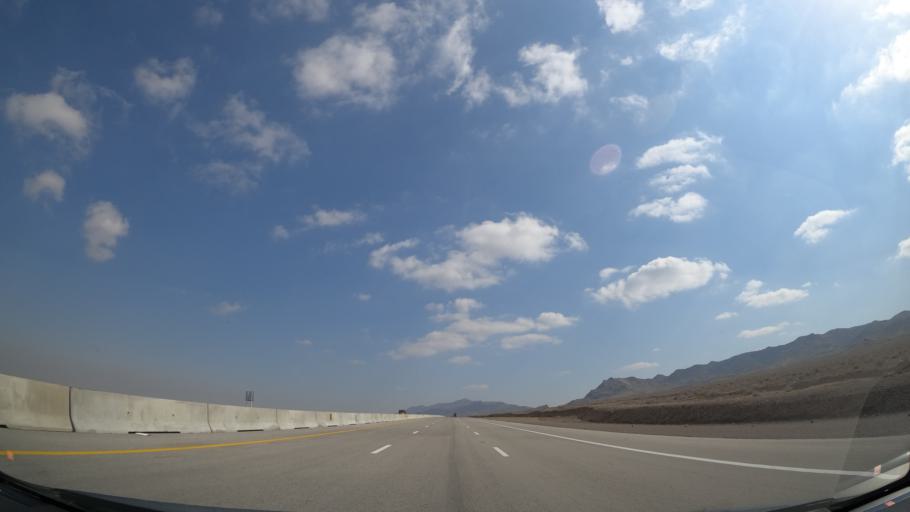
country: IR
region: Alborz
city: Eshtehard
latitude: 35.7109
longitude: 50.5951
